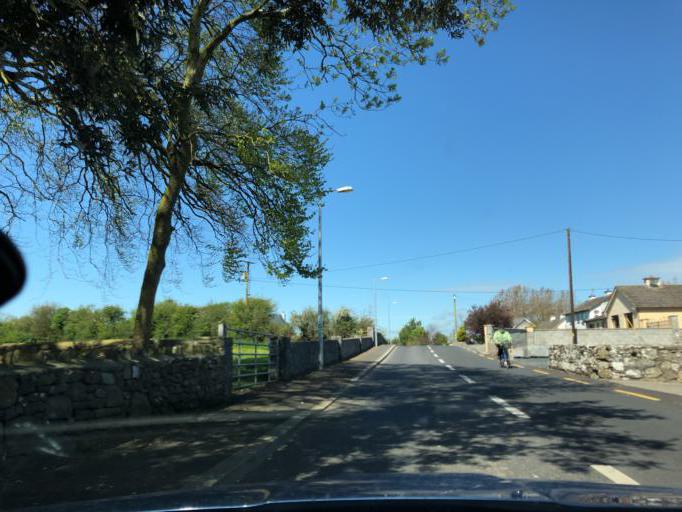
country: IE
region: Connaught
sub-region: County Galway
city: Portumna
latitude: 53.1534
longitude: -8.3797
